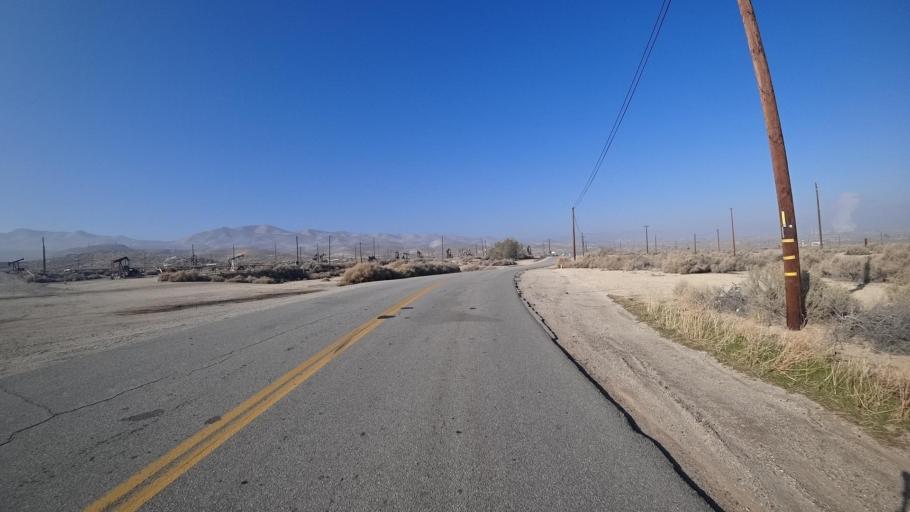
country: US
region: California
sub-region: Kern County
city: Taft Heights
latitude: 35.1869
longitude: -119.5639
